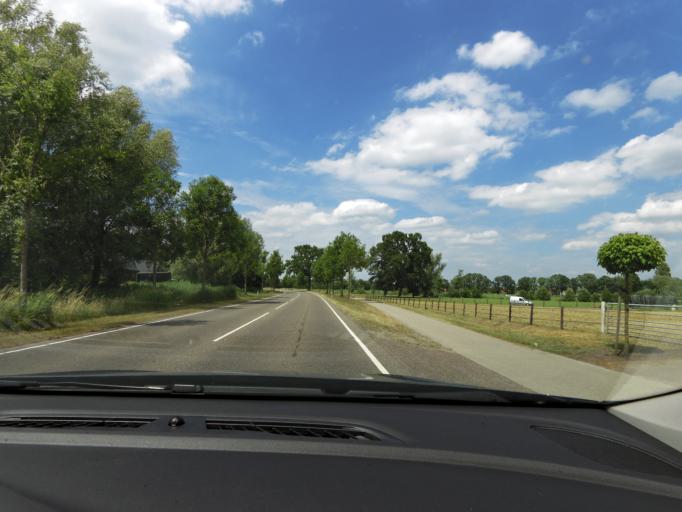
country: NL
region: North Brabant
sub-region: Gemeente Baarle-Nassau
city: Baarle-Nassau
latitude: 51.4947
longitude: 4.8745
